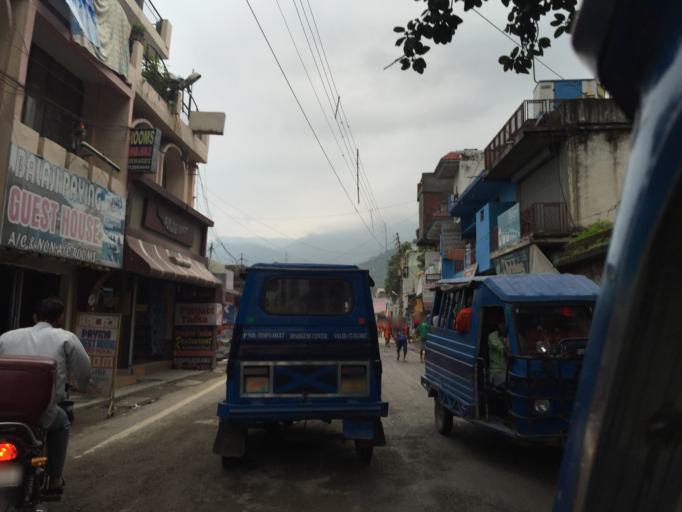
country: IN
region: Uttarakhand
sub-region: Dehradun
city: Rishikesh
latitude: 30.1130
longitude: 78.3029
